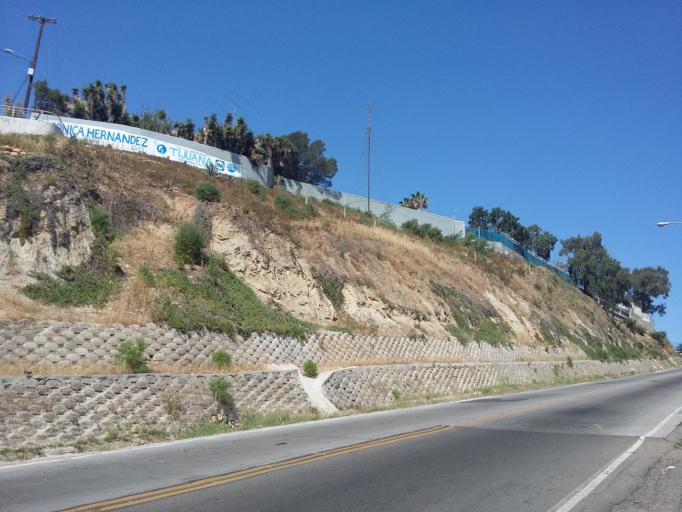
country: MX
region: Baja California
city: Tijuana
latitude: 32.5317
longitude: -117.0502
